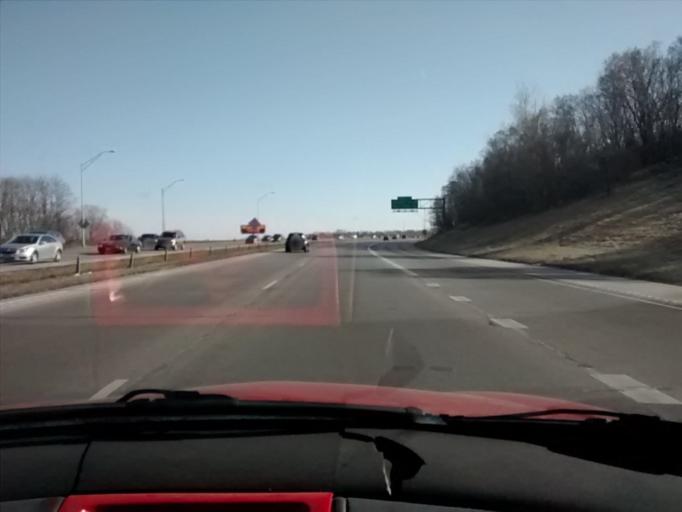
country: US
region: Nebraska
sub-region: Douglas County
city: Omaha
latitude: 41.1893
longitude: -95.9390
